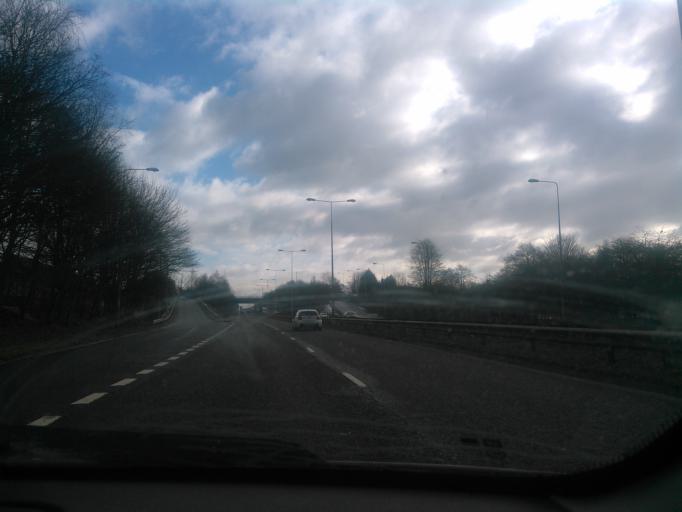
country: GB
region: England
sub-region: Staffordshire
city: Longton
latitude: 52.9684
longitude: -2.0811
